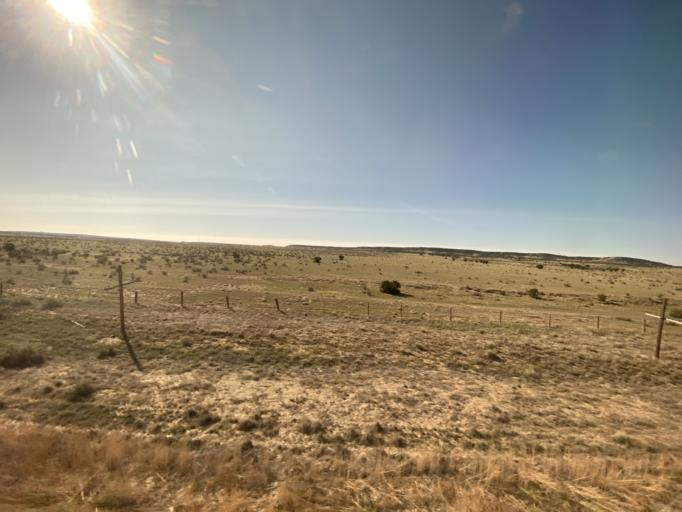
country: US
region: Colorado
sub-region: Otero County
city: Fowler
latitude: 37.5660
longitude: -104.0756
